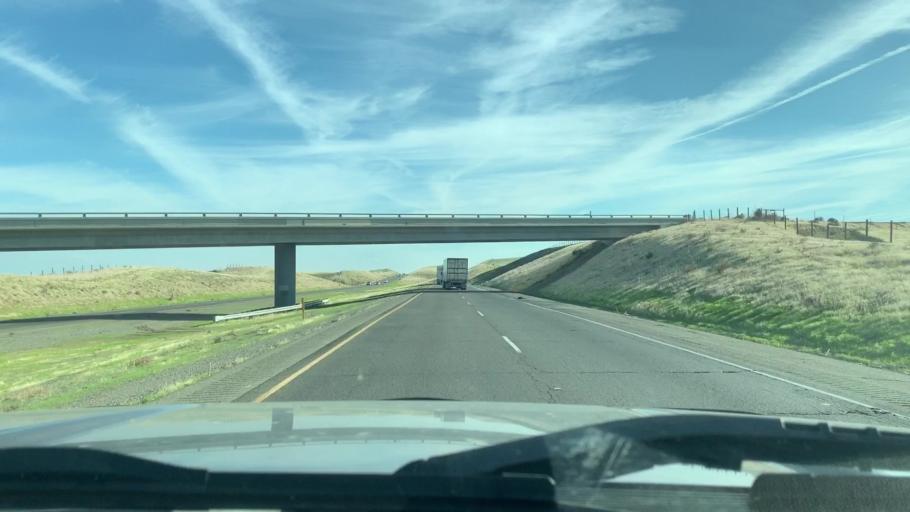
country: US
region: California
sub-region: Fresno County
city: Coalinga
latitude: 36.3311
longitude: -120.3008
